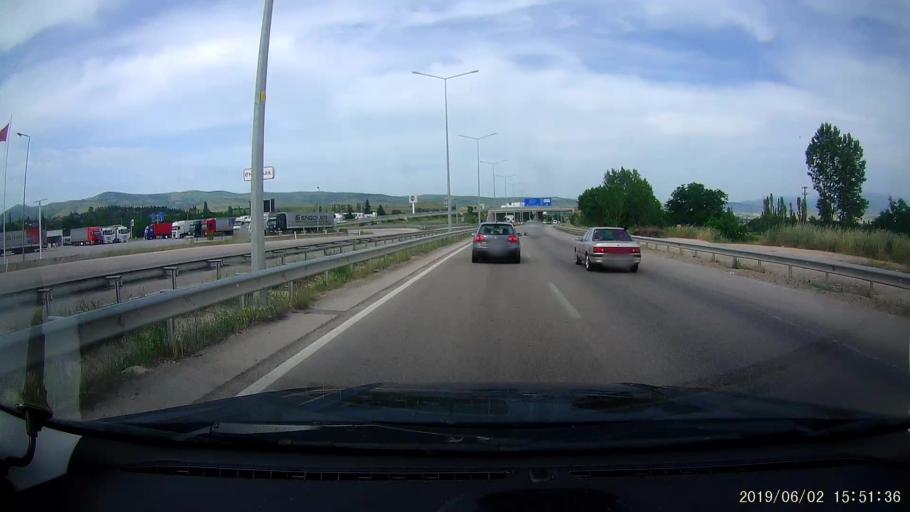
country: TR
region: Amasya
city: Merzifon
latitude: 40.8687
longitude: 35.4973
